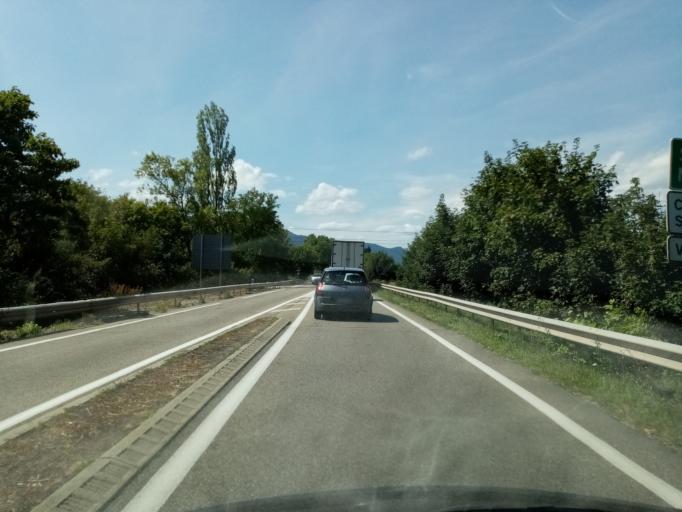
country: FR
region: Alsace
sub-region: Departement du Bas-Rhin
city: Chatenois
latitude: 48.2719
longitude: 7.4150
